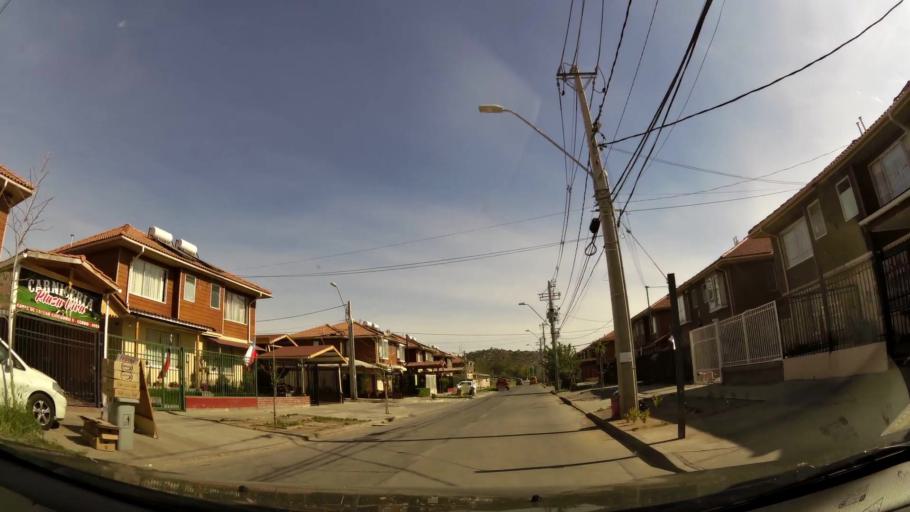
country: CL
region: Santiago Metropolitan
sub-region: Provincia de Cordillera
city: Puente Alto
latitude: -33.5917
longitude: -70.5483
